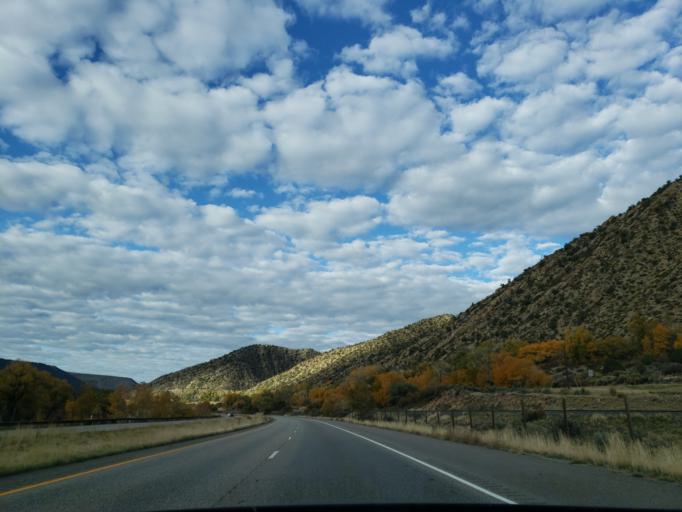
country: US
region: Colorado
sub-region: Garfield County
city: New Castle
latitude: 39.5691
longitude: -107.5422
